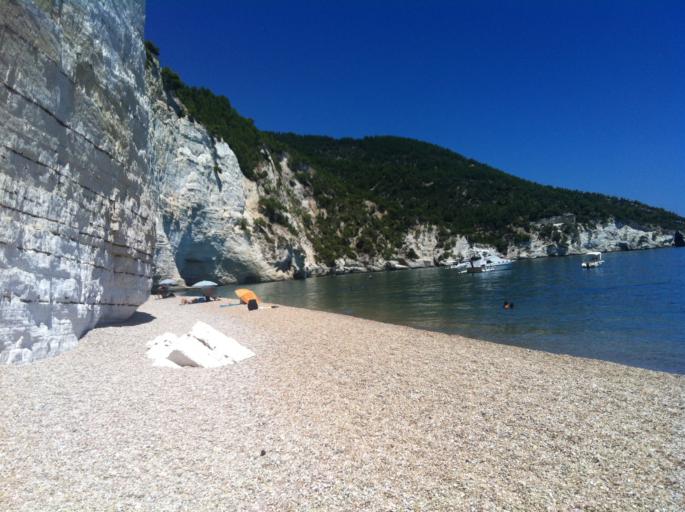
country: IT
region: Apulia
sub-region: Provincia di Foggia
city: Vieste
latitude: 41.7644
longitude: 16.1661
